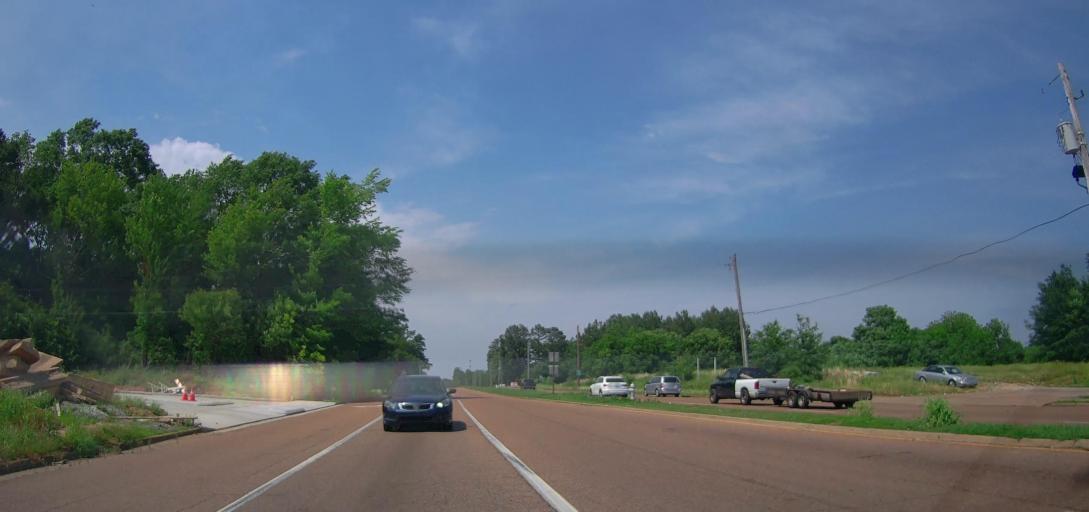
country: US
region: Mississippi
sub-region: De Soto County
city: Olive Branch
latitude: 34.9950
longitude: -89.8308
